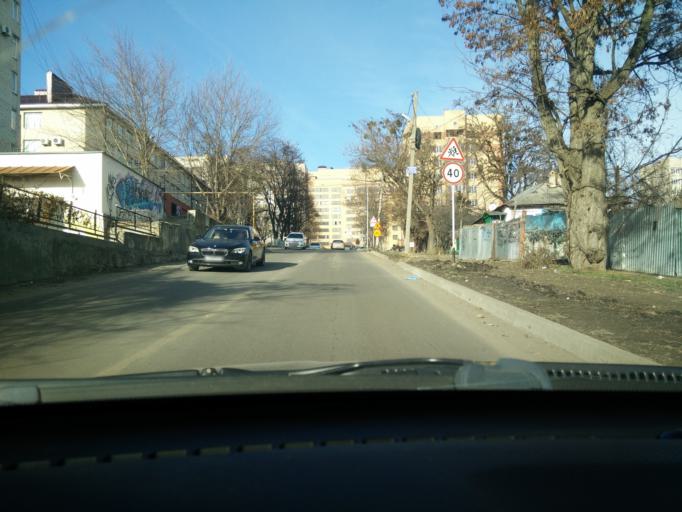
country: RU
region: Stavropol'skiy
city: Stavropol'
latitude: 45.0367
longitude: 41.9802
